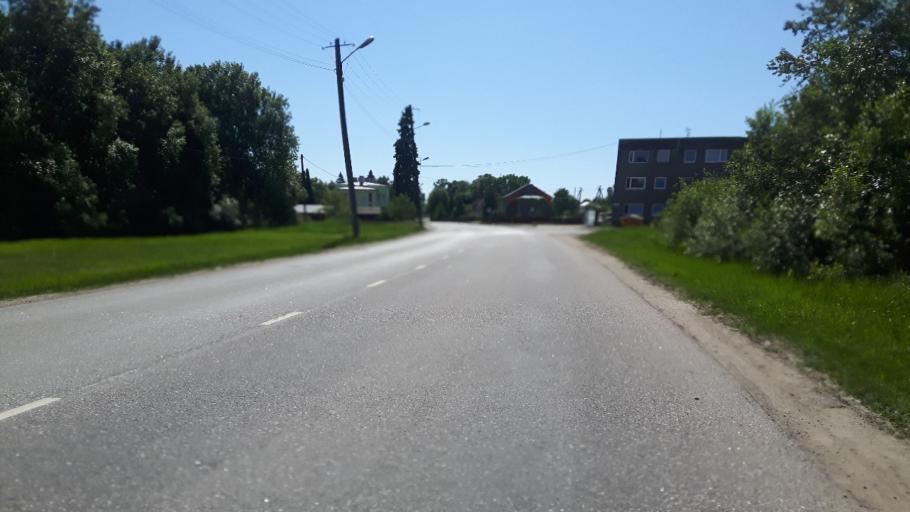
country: EE
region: Paernumaa
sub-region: Sindi linn
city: Sindi
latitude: 58.4132
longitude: 24.6707
